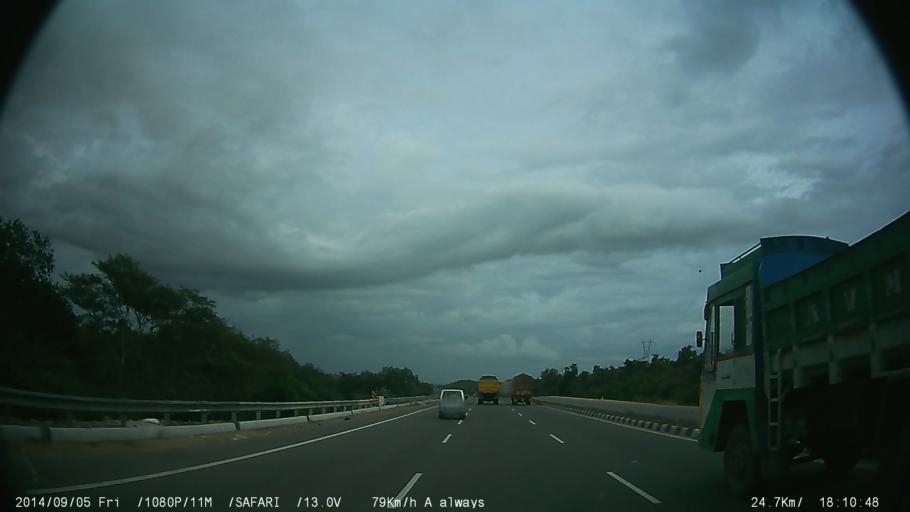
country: IN
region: Tamil Nadu
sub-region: Krishnagiri
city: Hosur
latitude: 12.7060
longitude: 77.9032
